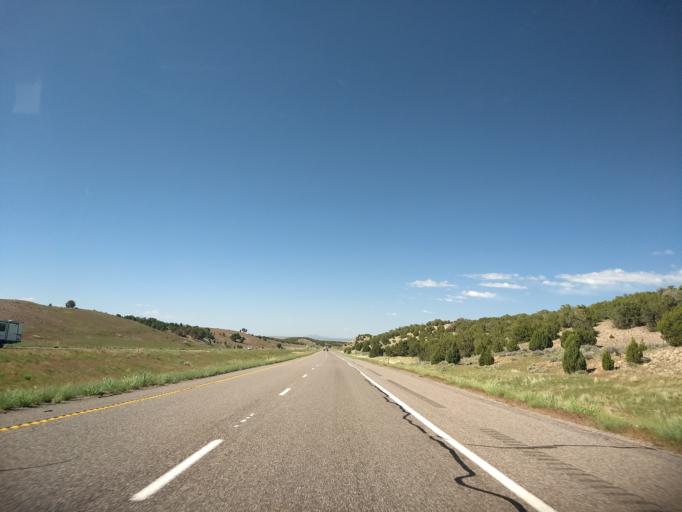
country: US
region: Utah
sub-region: Millard County
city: Fillmore
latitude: 38.7091
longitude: -112.5997
